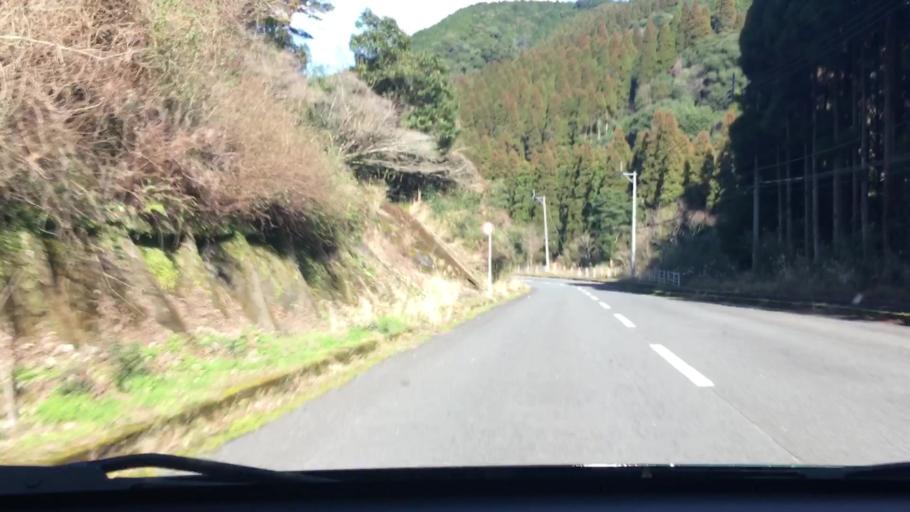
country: JP
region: Kagoshima
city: Satsumasendai
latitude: 31.7492
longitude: 130.4103
